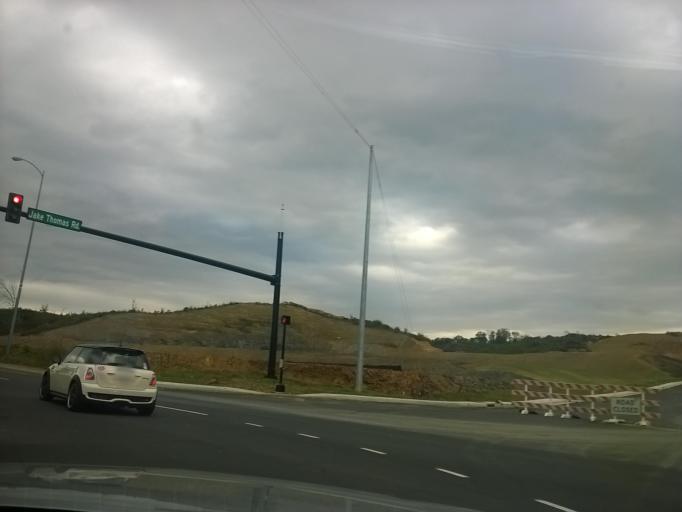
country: US
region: Tennessee
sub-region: Sevier County
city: Pigeon Forge
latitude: 35.7976
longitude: -83.5604
